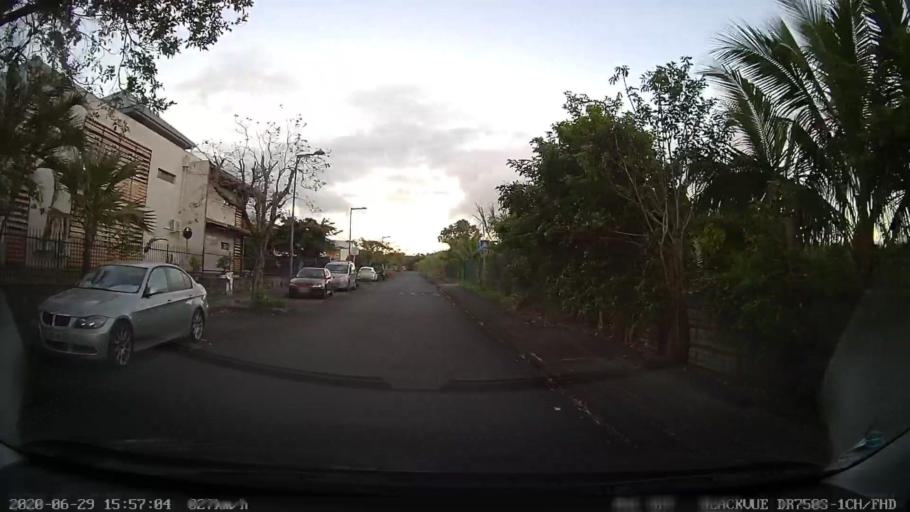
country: RE
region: Reunion
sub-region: Reunion
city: Bras-Panon
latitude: -20.9989
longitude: 55.6926
